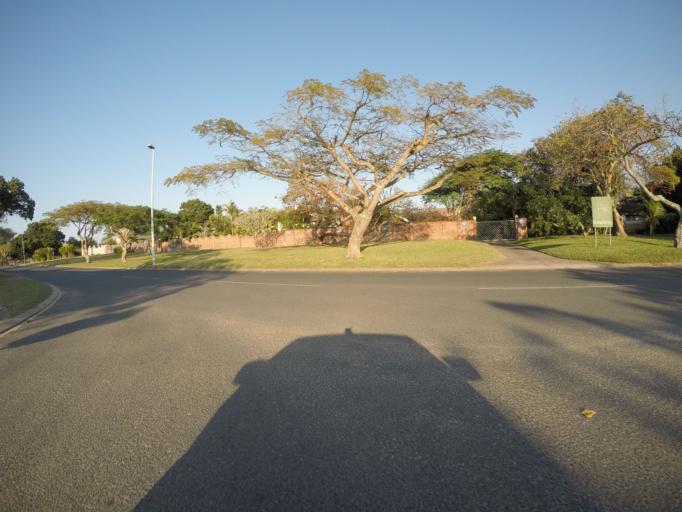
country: ZA
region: KwaZulu-Natal
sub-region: uThungulu District Municipality
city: Richards Bay
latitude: -28.7800
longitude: 32.1112
